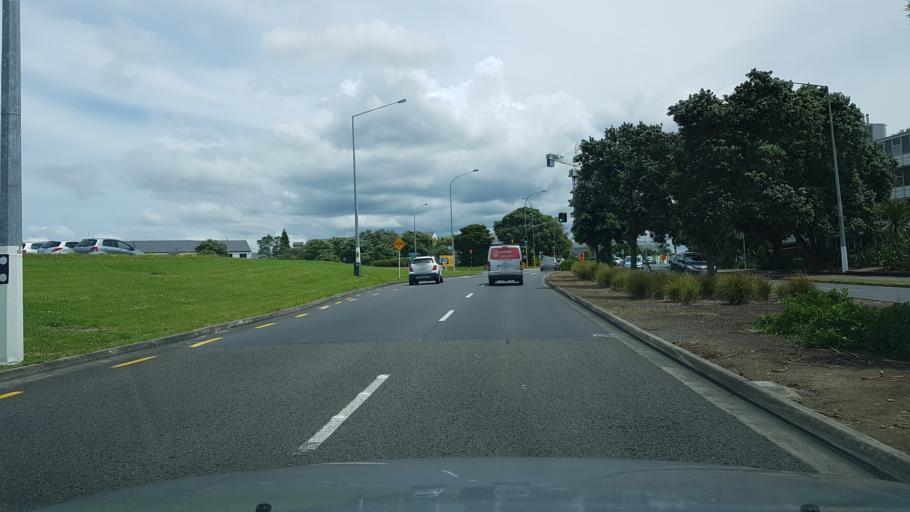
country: NZ
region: Auckland
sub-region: Auckland
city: North Shore
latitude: -36.8000
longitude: 174.7584
